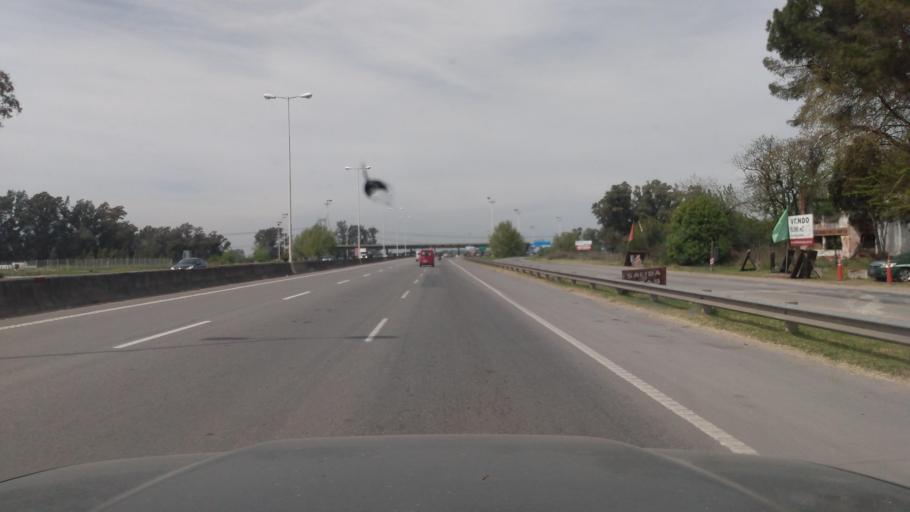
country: AR
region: Buenos Aires
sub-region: Partido de Pilar
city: Pilar
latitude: -34.4002
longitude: -59.0174
